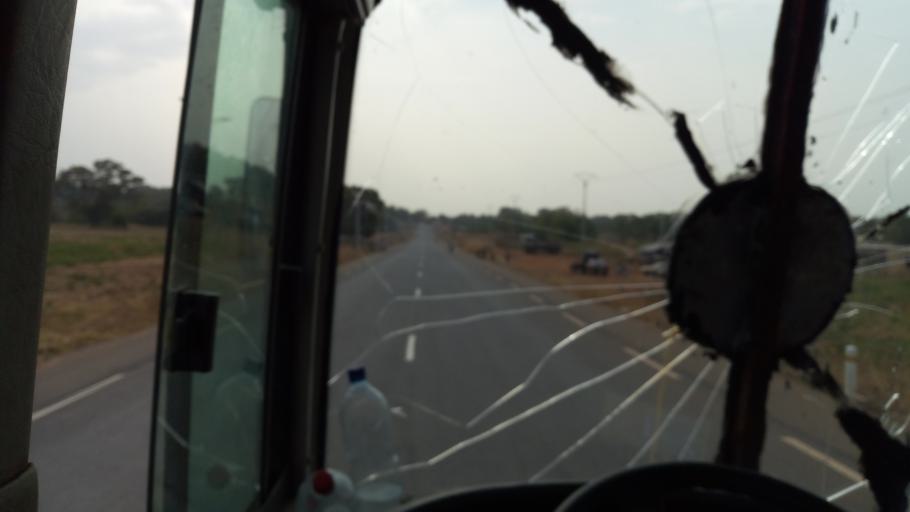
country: TG
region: Kara
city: Bafilo
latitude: 9.3631
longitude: 1.2456
